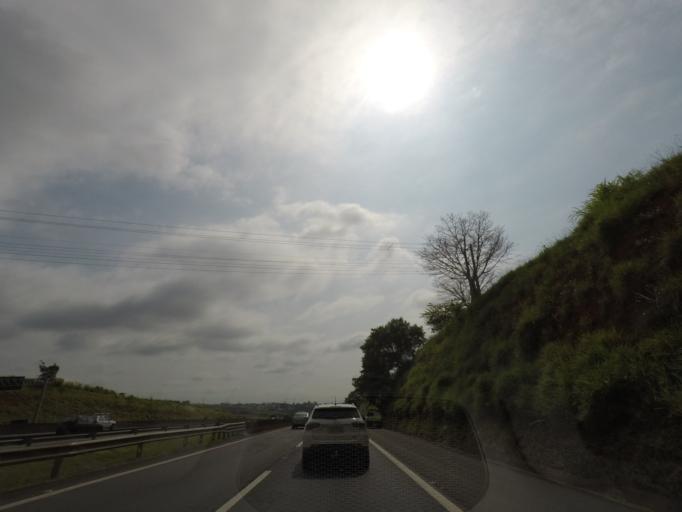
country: BR
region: Sao Paulo
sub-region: Campinas
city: Campinas
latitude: -22.8448
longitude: -47.0743
